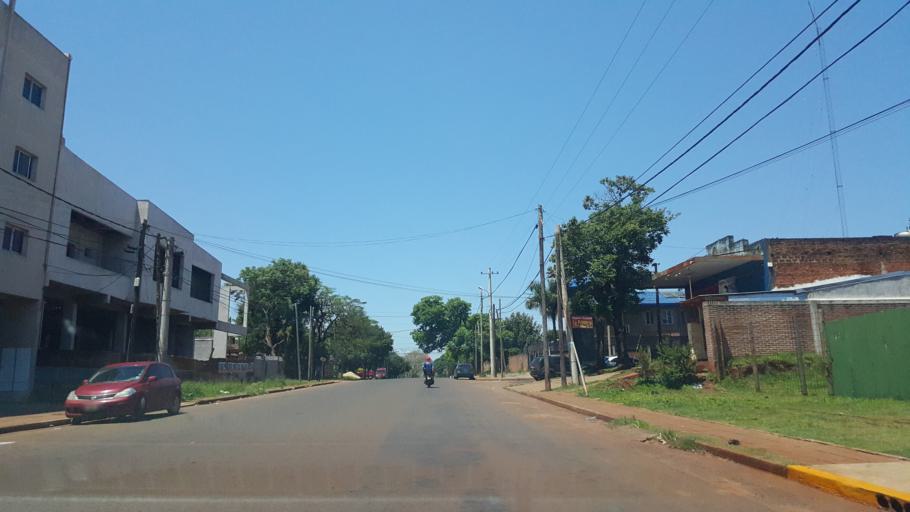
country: AR
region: Misiones
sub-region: Departamento de Capital
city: Posadas
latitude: -27.3825
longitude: -55.9166
